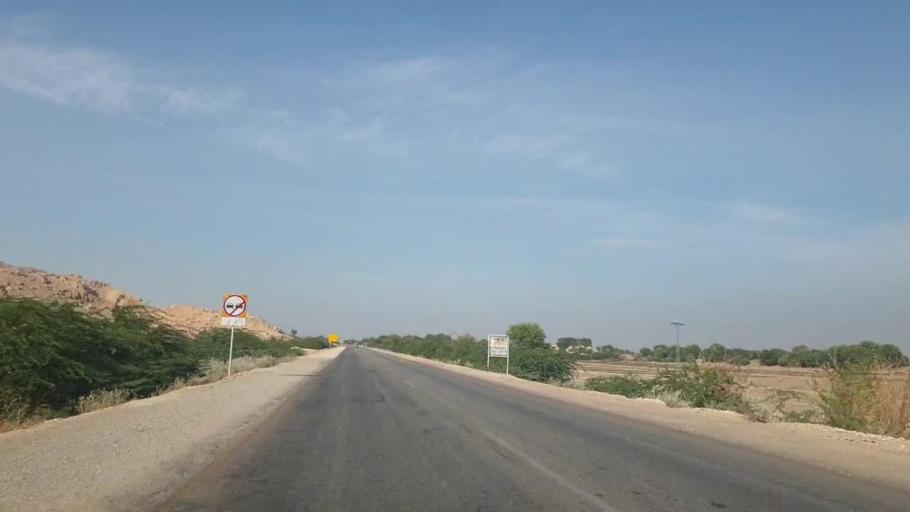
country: PK
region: Sindh
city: Sehwan
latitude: 26.3070
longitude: 67.8929
